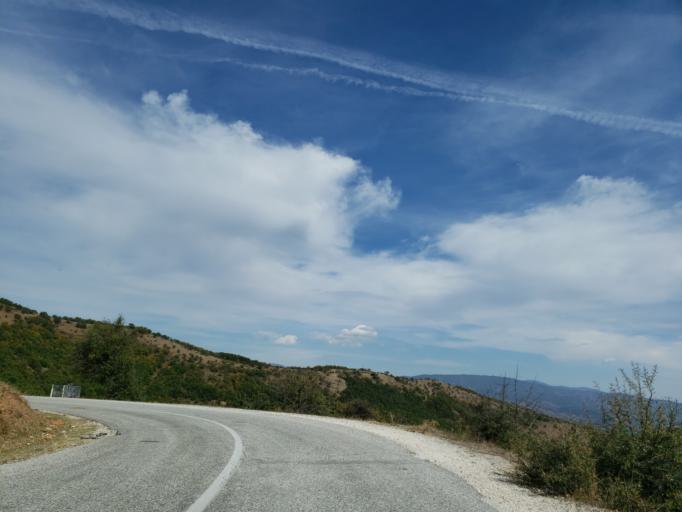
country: GR
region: Thessaly
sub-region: Trikala
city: Kastraki
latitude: 39.7444
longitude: 21.6589
